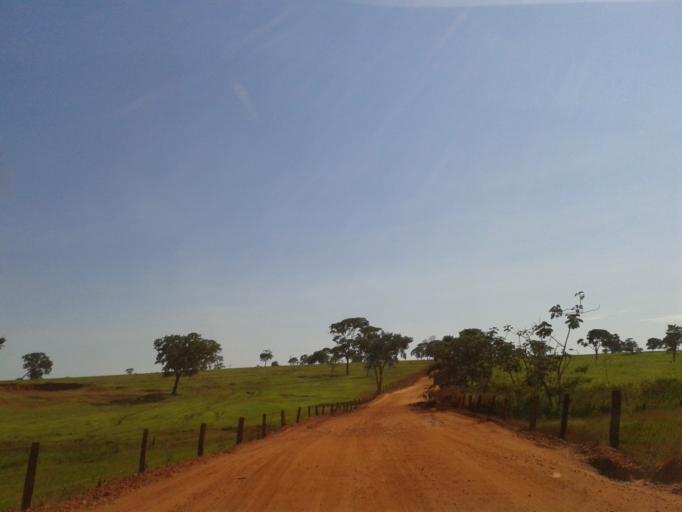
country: BR
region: Minas Gerais
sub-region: Santa Vitoria
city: Santa Vitoria
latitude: -19.1016
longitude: -50.5065
